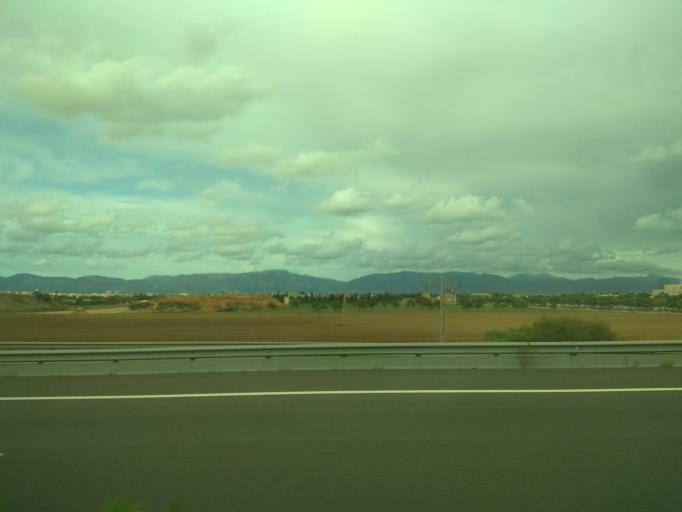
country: ES
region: Balearic Islands
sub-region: Illes Balears
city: Palma
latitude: 39.5697
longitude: 2.7000
